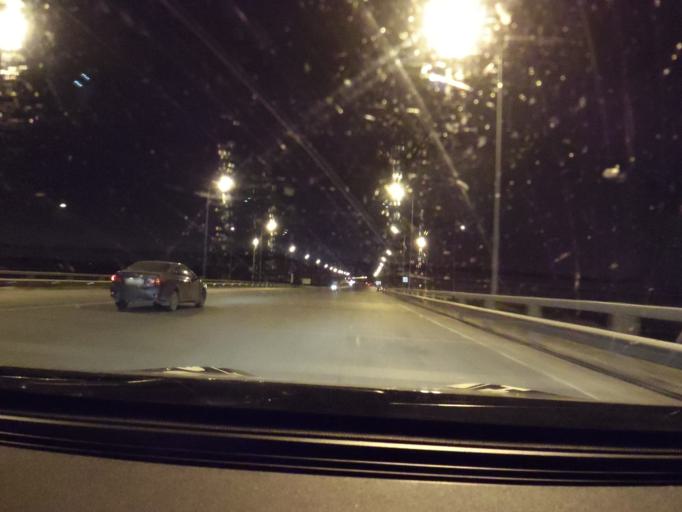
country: RU
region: Tatarstan
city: Vysokaya Gora
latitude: 55.7993
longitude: 49.3385
